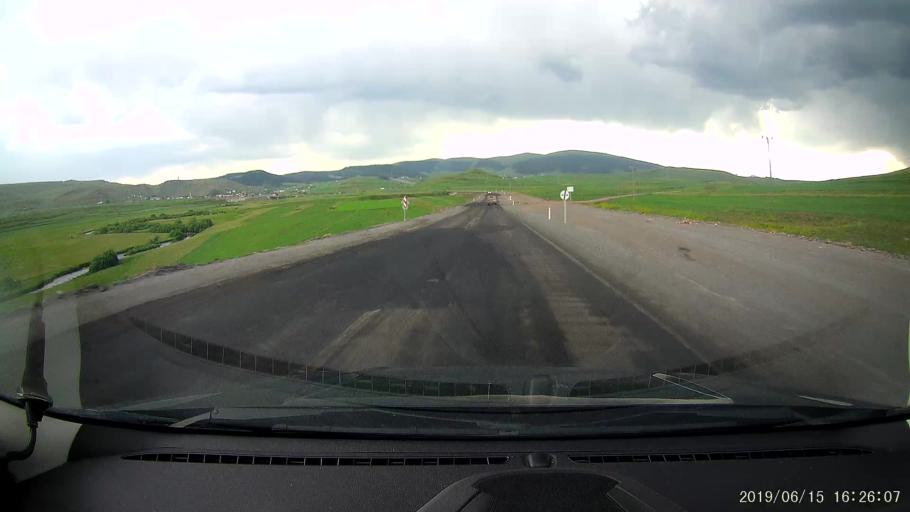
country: TR
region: Ardahan
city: Hanak
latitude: 41.1456
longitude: 42.8634
